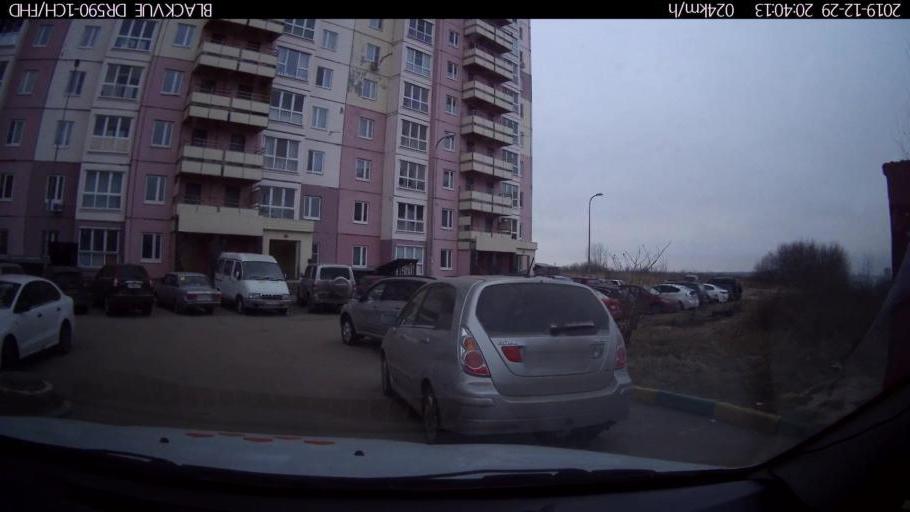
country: RU
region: Nizjnij Novgorod
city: Bor
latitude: 56.3159
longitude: 44.0601
